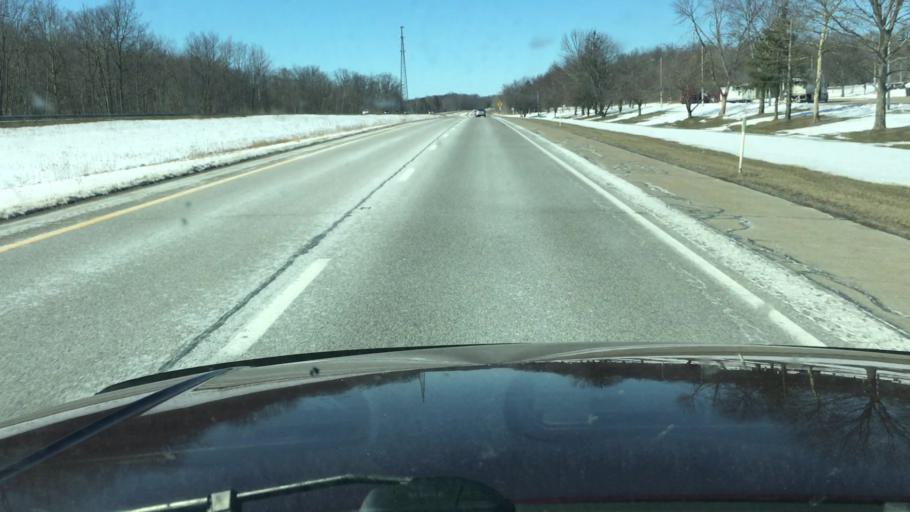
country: US
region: Pennsylvania
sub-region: Mercer County
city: Stoneboro
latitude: 41.4541
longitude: -80.1621
